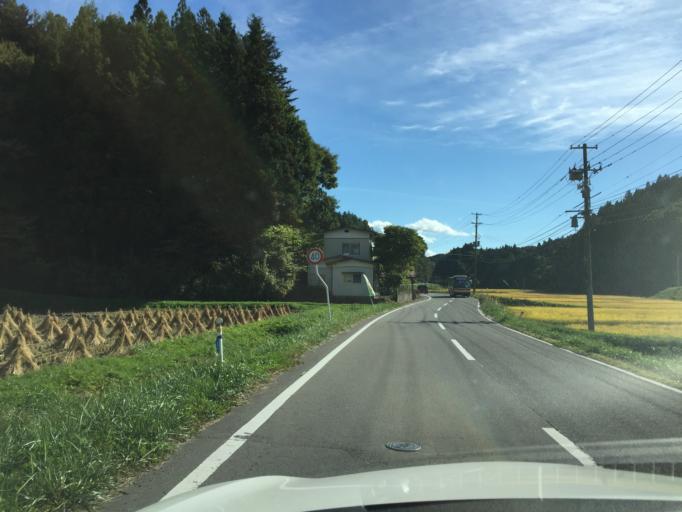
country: JP
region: Fukushima
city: Ishikawa
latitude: 37.2156
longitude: 140.5813
